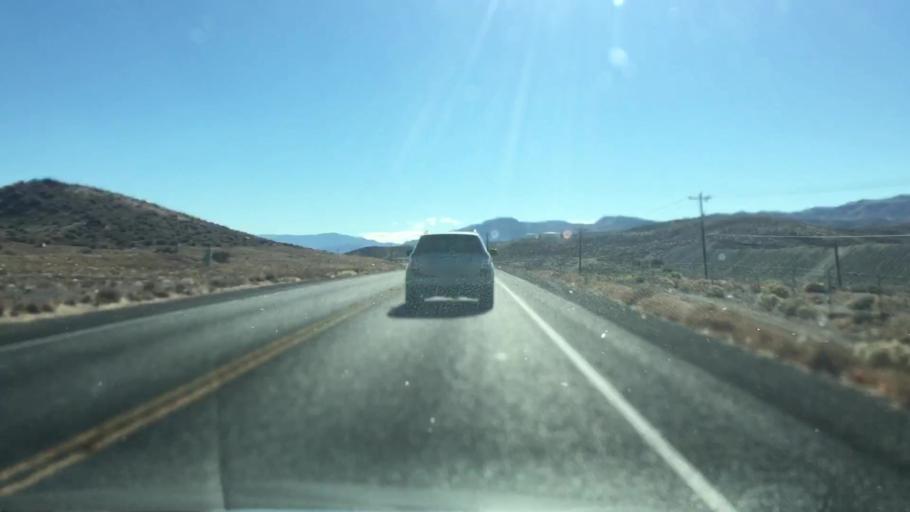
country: US
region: Nevada
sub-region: Lyon County
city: Yerington
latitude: 39.0127
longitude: -119.1826
